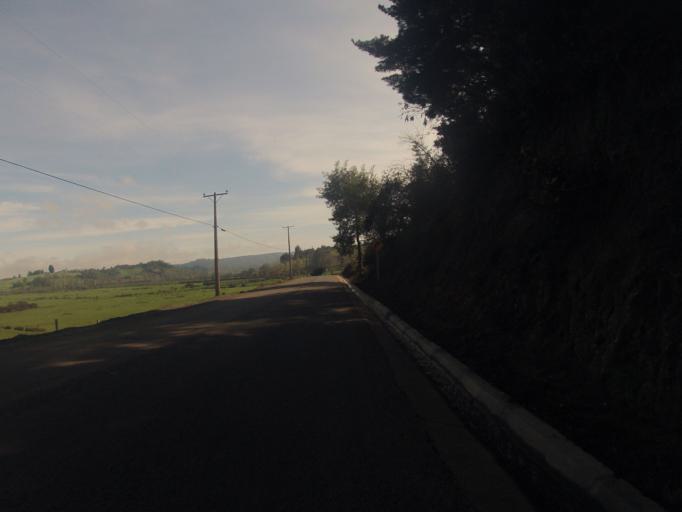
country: CL
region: Araucania
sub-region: Provincia de Cautin
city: Temuco
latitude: -38.7136
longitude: -72.5992
